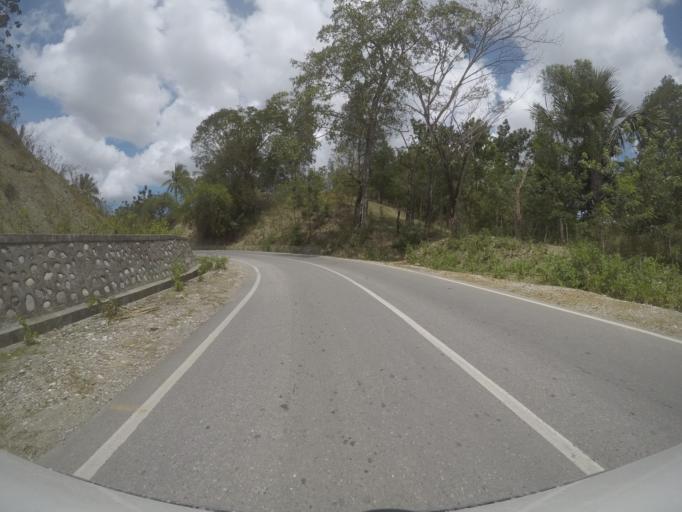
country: TL
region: Viqueque
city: Viqueque
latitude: -8.8755
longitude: 126.3758
